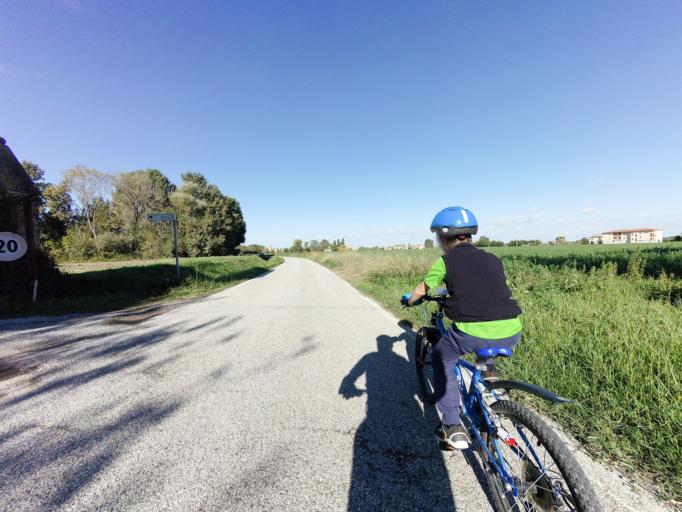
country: IT
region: Emilia-Romagna
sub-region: Provincia di Bologna
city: Bentivoglio
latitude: 44.5970
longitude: 11.4139
